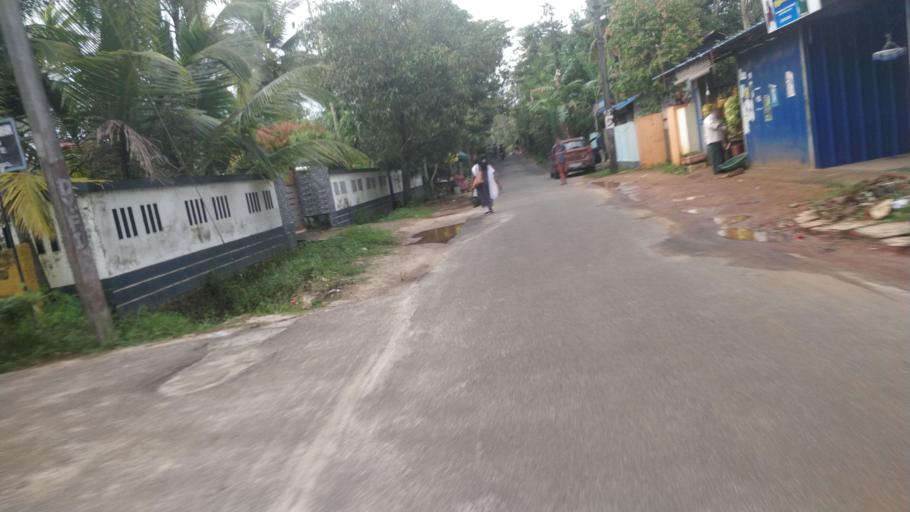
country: IN
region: Kerala
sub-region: Alappuzha
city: Vayalar
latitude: 9.6975
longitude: 76.3474
